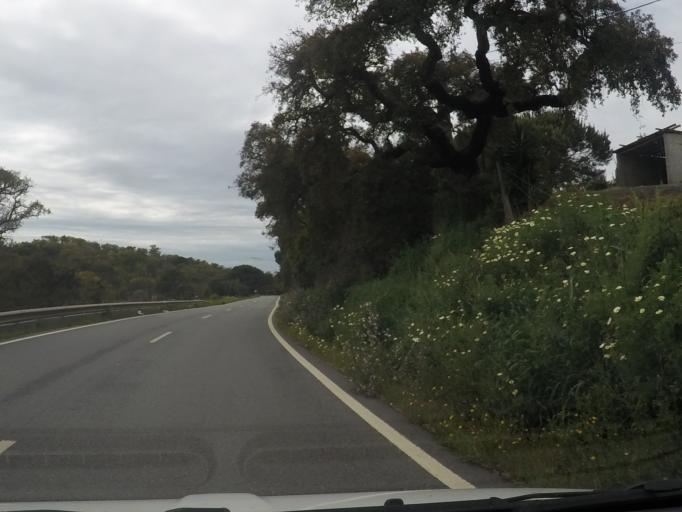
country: PT
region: Setubal
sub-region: Sines
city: Porto Covo
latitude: 37.8683
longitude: -8.7385
